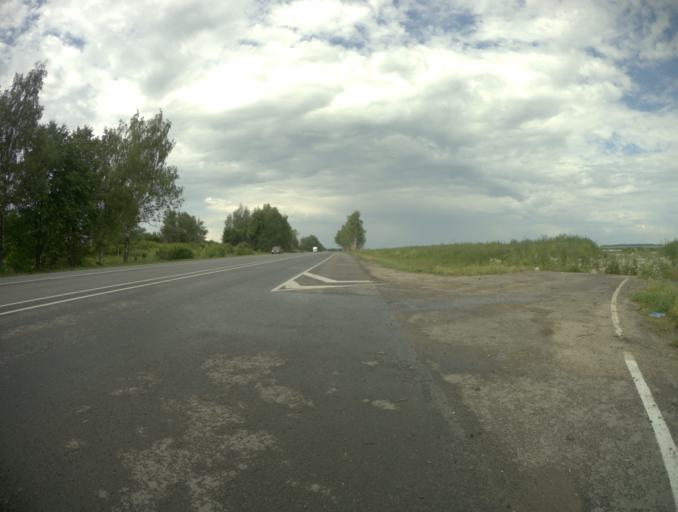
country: RU
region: Vladimir
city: Bogolyubovo
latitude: 56.2992
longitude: 40.4701
